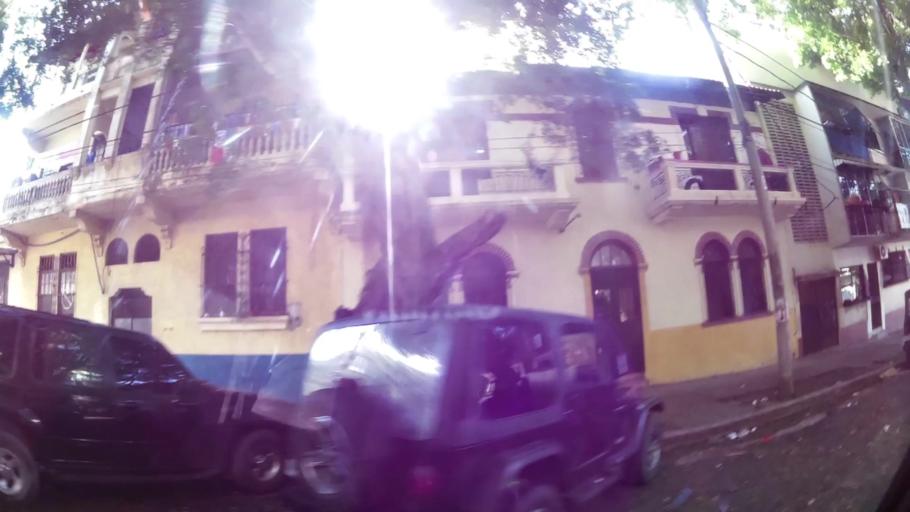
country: PA
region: Panama
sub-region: Distrito de Panama
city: Ancon
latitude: 8.9560
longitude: -79.5435
